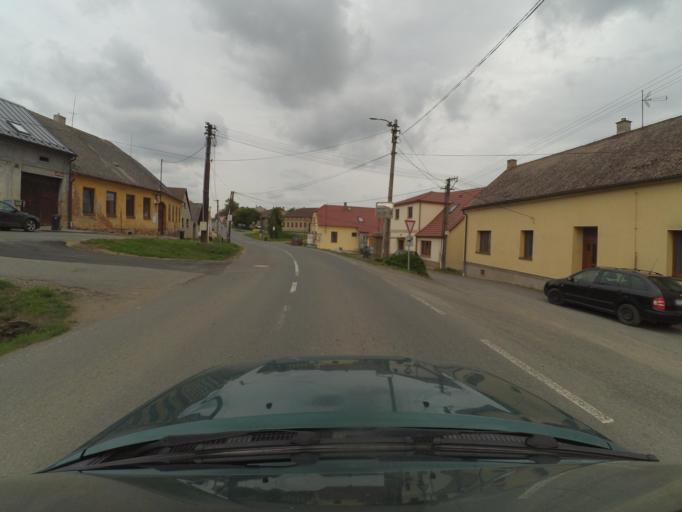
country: CZ
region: Plzensky
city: Kozlany
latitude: 50.0270
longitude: 13.5745
